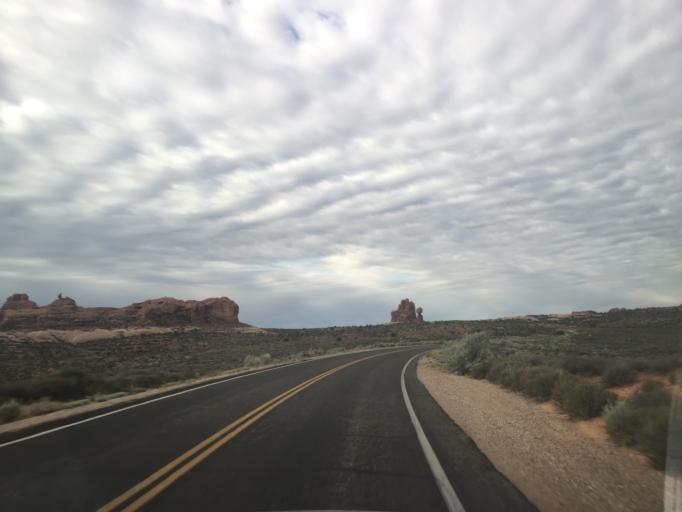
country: US
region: Utah
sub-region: Grand County
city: Moab
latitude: 38.7151
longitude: -109.5565
